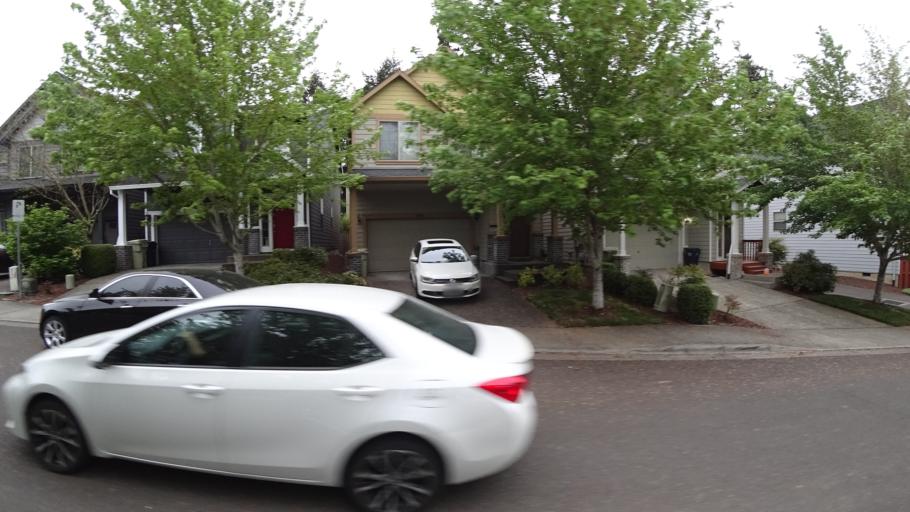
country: US
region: Oregon
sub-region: Washington County
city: Aloha
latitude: 45.5120
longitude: -122.8834
